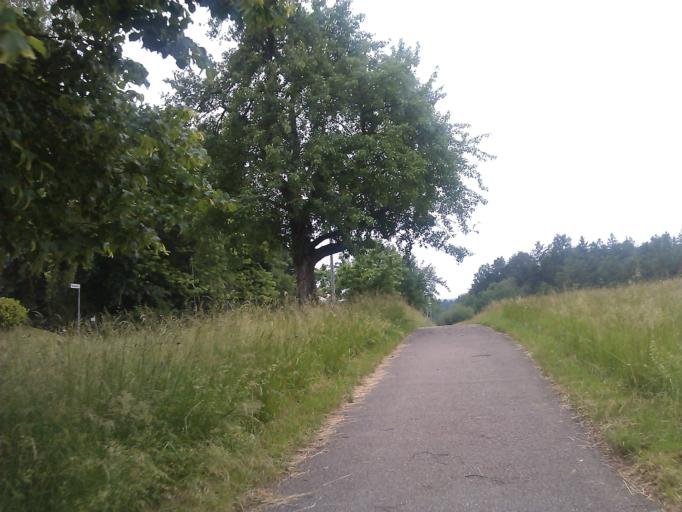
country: DE
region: Baden-Wuerttemberg
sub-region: Regierungsbezirk Stuttgart
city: Mainhardt
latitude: 49.0702
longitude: 9.5563
